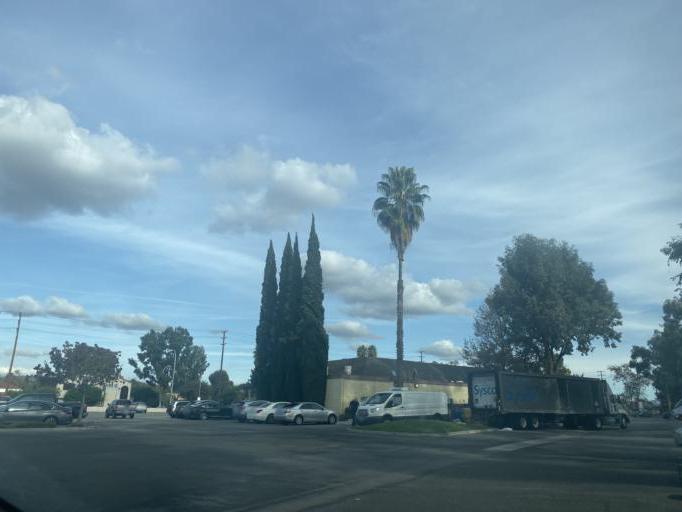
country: US
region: California
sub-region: Orange County
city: Brea
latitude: 33.9107
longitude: -117.8876
